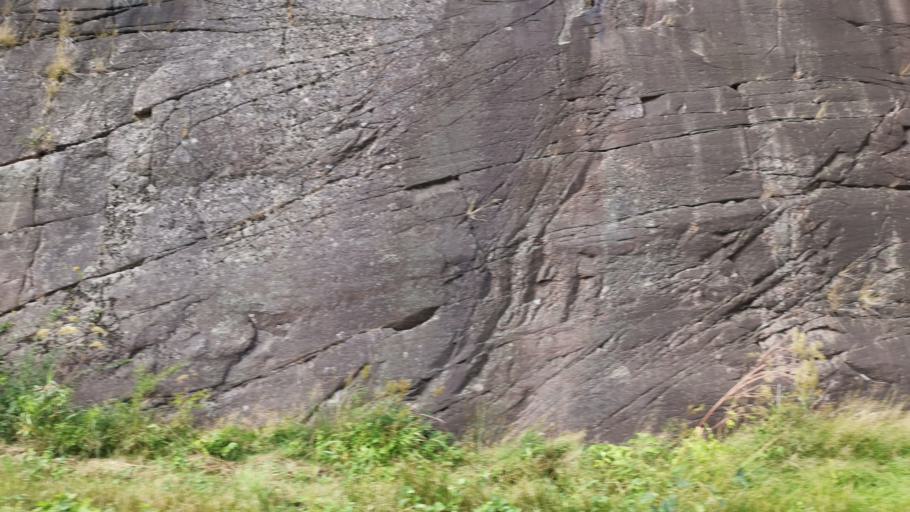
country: SE
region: Vaestra Goetaland
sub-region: Lysekils Kommun
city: Brastad
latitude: 58.4634
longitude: 11.4576
